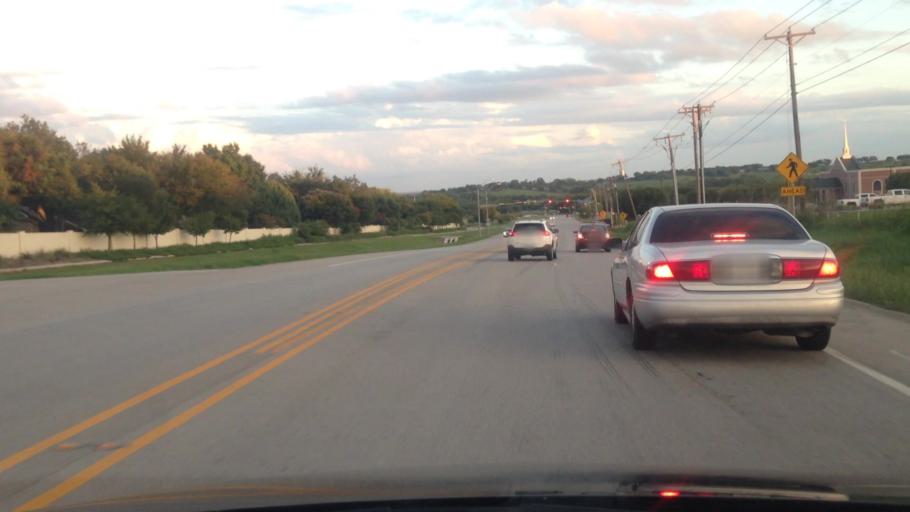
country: US
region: Texas
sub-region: Tarrant County
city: Benbrook
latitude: 32.6683
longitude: -97.4903
